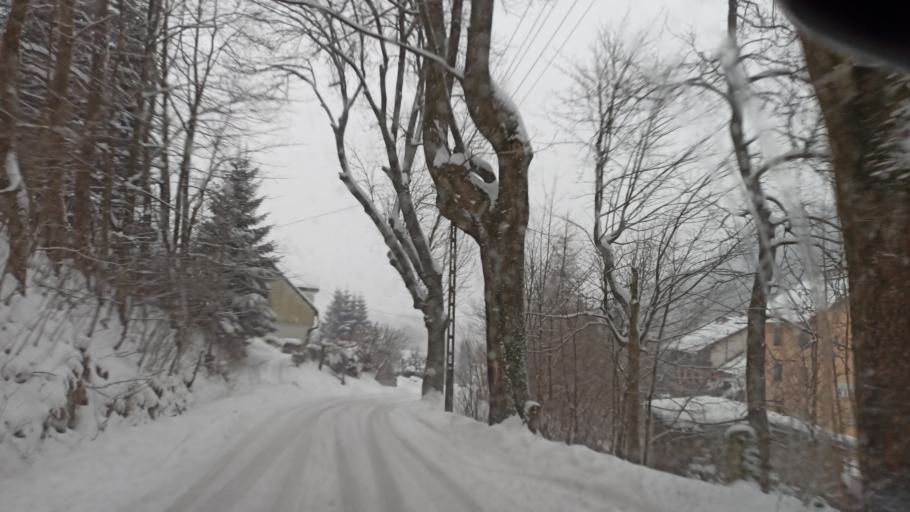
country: PL
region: Lower Silesian Voivodeship
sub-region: Powiat klodzki
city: Ludwikowice Klodzkie
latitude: 50.6565
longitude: 16.4744
